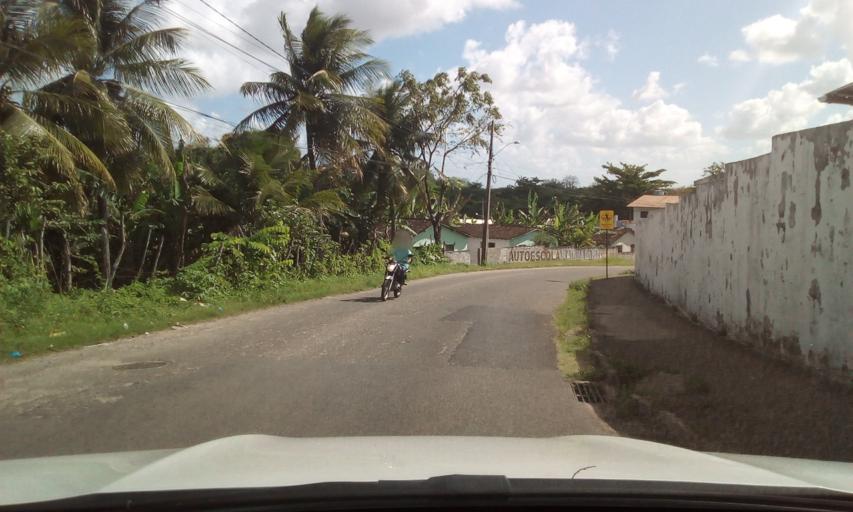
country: BR
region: Paraiba
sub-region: Joao Pessoa
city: Joao Pessoa
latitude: -7.1294
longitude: -34.8863
